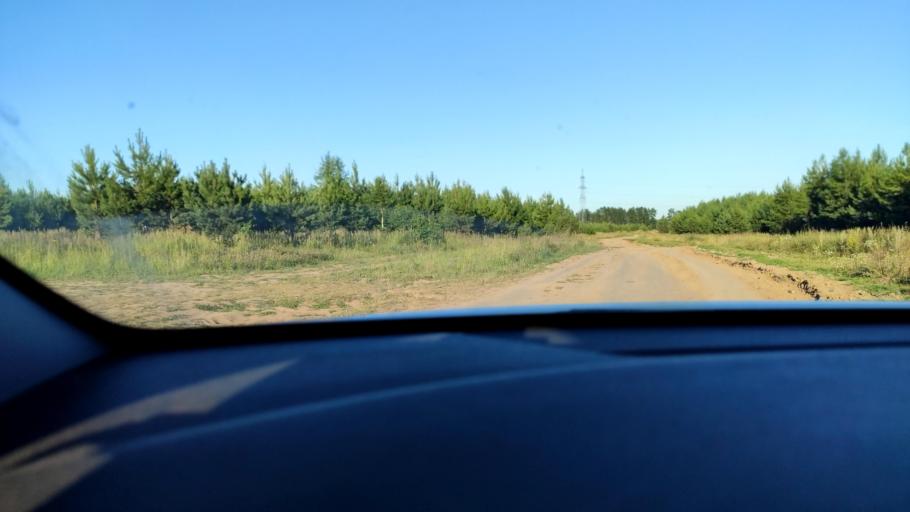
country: RU
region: Tatarstan
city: Vysokaya Gora
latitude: 55.8223
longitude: 49.2428
